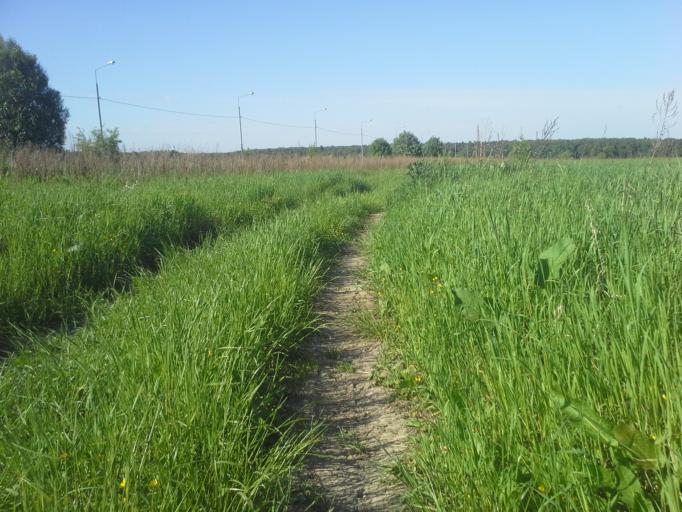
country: RU
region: Moskovskaya
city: Dubrovitsy
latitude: 55.4701
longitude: 37.4148
